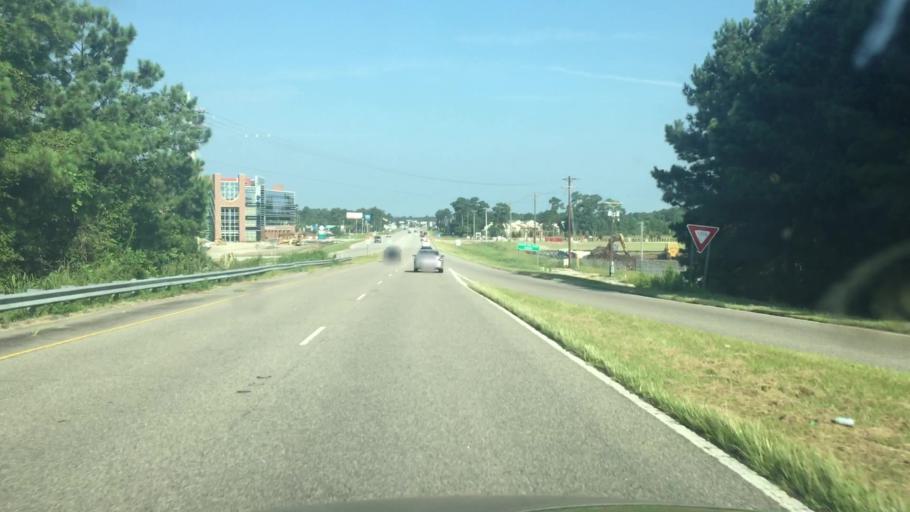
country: US
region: South Carolina
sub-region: Horry County
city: Little River
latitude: 33.8649
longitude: -78.6595
